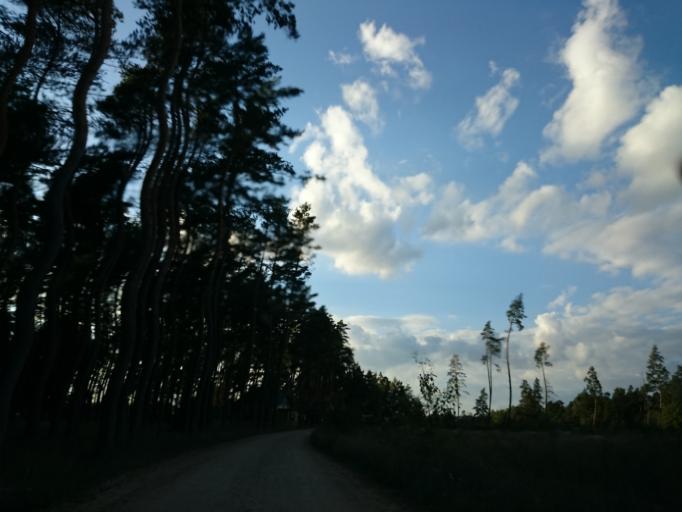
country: LV
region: Adazi
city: Adazi
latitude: 57.0636
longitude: 24.2777
